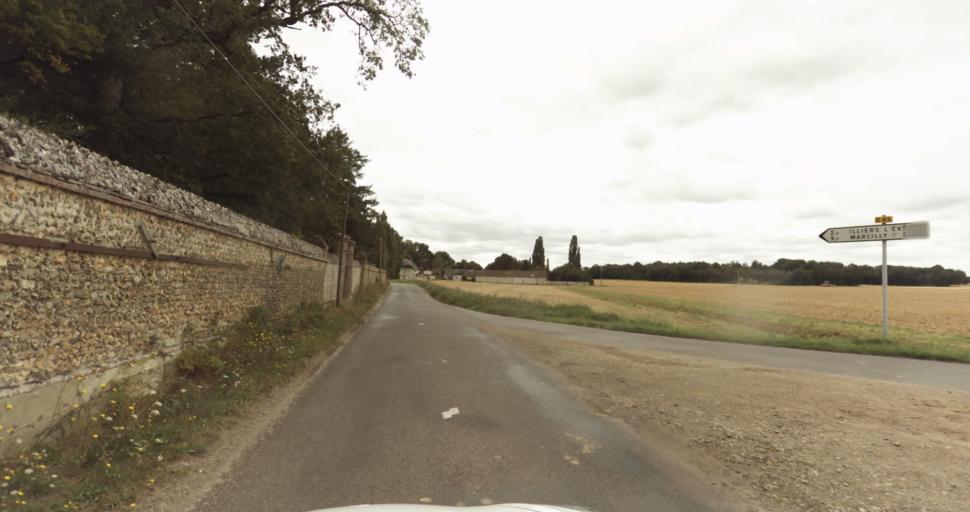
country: FR
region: Centre
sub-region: Departement d'Eure-et-Loir
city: Saint-Lubin-des-Joncherets
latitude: 48.8196
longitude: 1.2350
